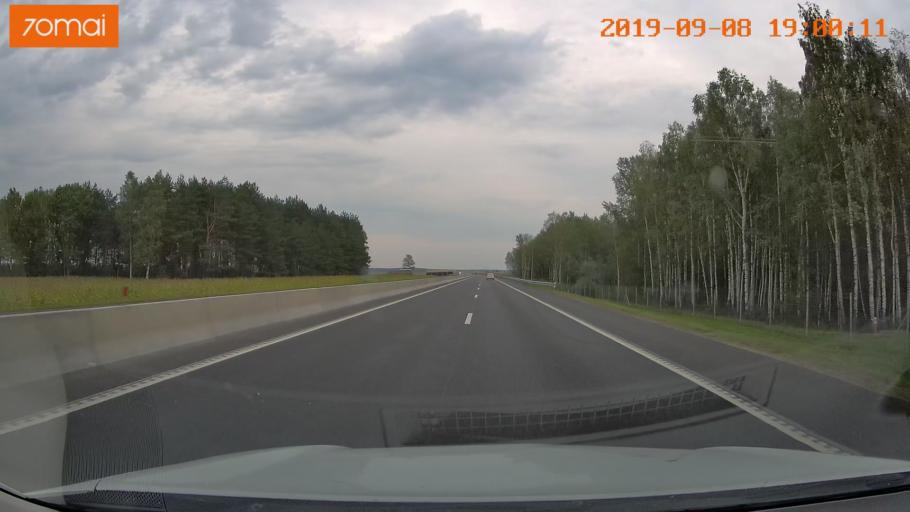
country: BY
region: Grodnenskaya
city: Lyubcha
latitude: 53.9052
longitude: 26.0114
